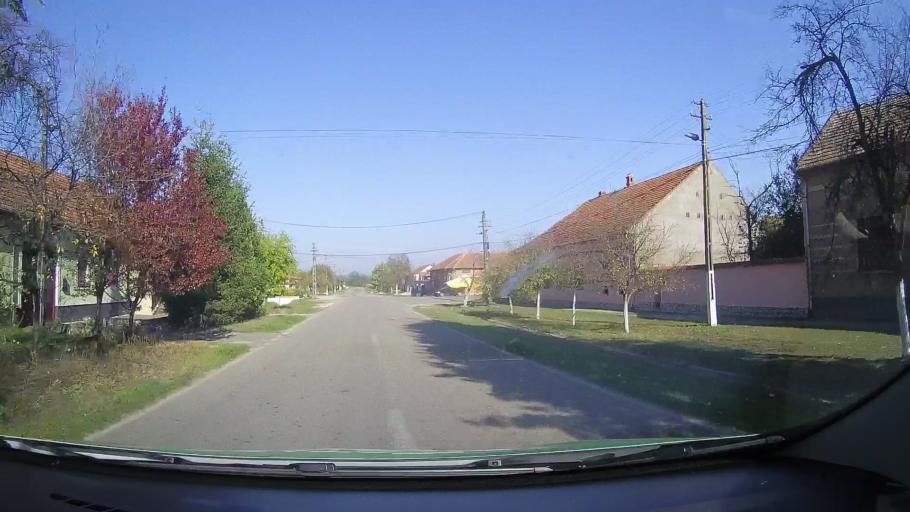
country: RO
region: Timis
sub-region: Comuna Curtea
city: Curtea
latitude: 45.8314
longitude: 22.3066
